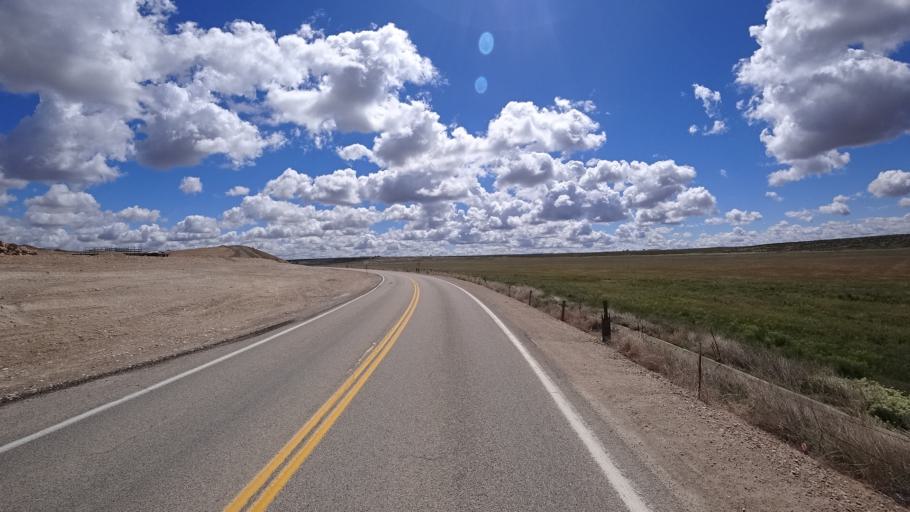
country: US
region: Idaho
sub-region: Ada County
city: Boise
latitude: 43.4851
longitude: -116.2516
